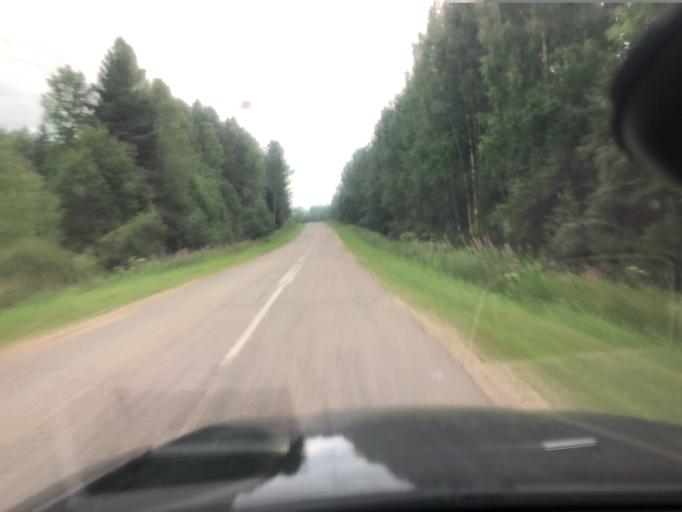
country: RU
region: Jaroslavl
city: Pereslavl'-Zalesskiy
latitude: 57.0353
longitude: 38.9070
